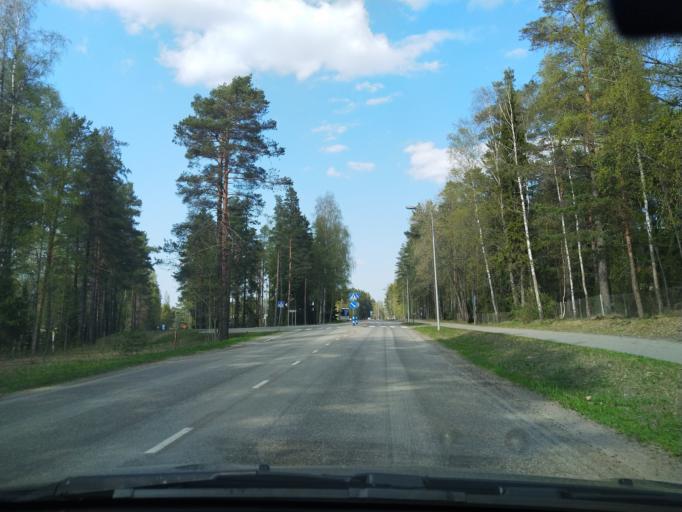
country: FI
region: Uusimaa
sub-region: Helsinki
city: Lohja
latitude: 60.1840
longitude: 23.9943
